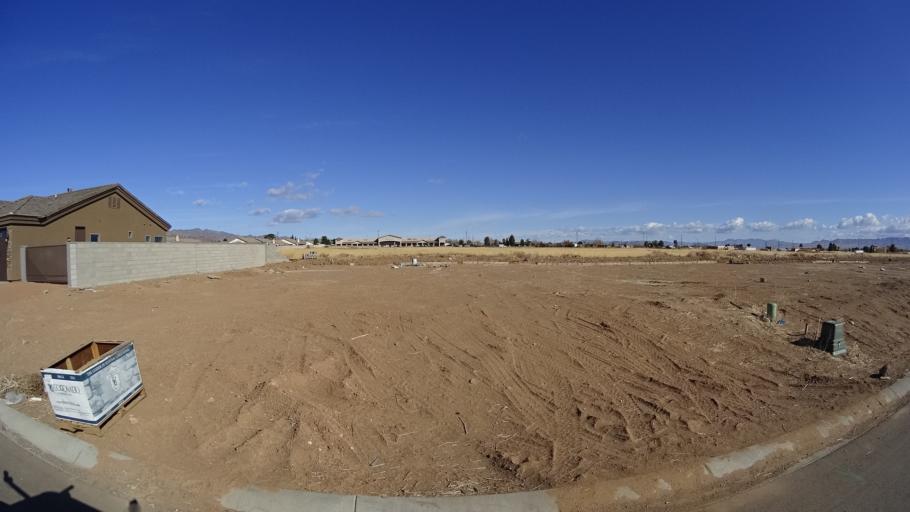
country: US
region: Arizona
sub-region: Mohave County
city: New Kingman-Butler
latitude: 35.2363
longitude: -114.0271
